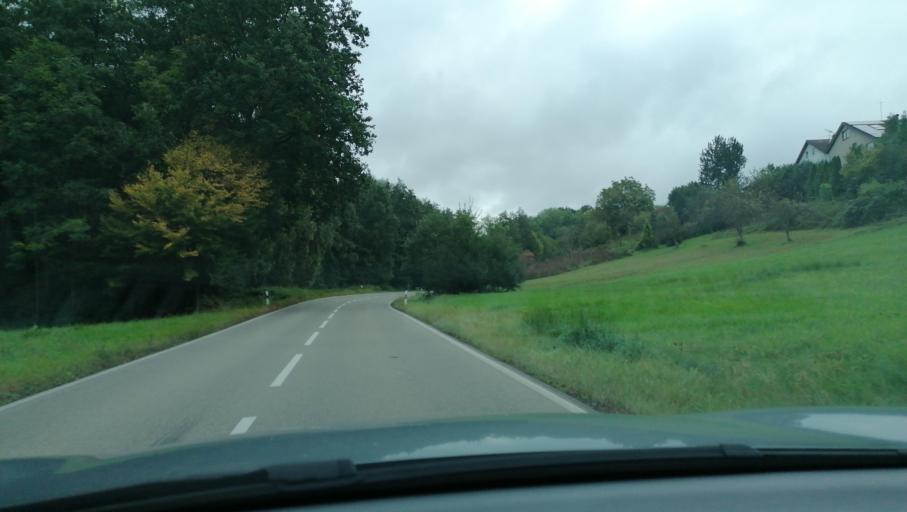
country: DE
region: Baden-Wuerttemberg
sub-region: Regierungsbezirk Stuttgart
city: Winterbach
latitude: 48.8465
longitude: 9.4575
